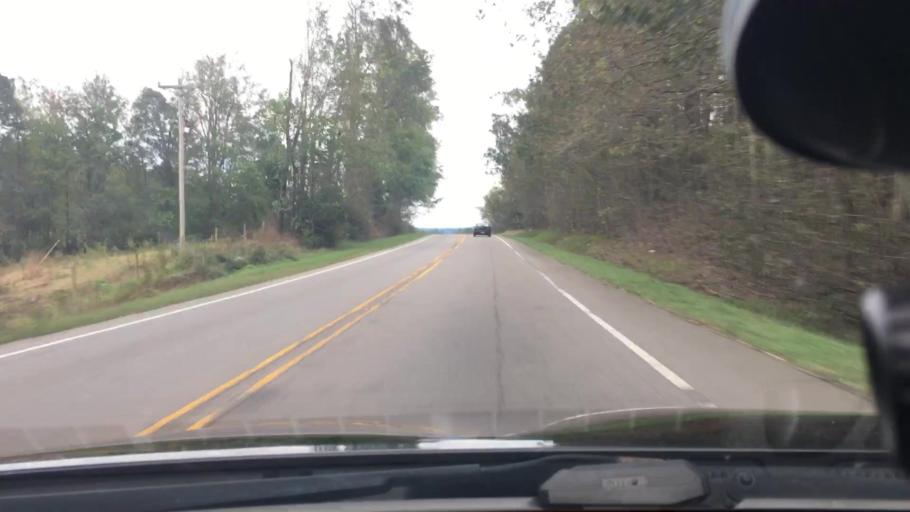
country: US
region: North Carolina
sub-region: Moore County
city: Robbins
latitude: 35.3922
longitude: -79.5197
